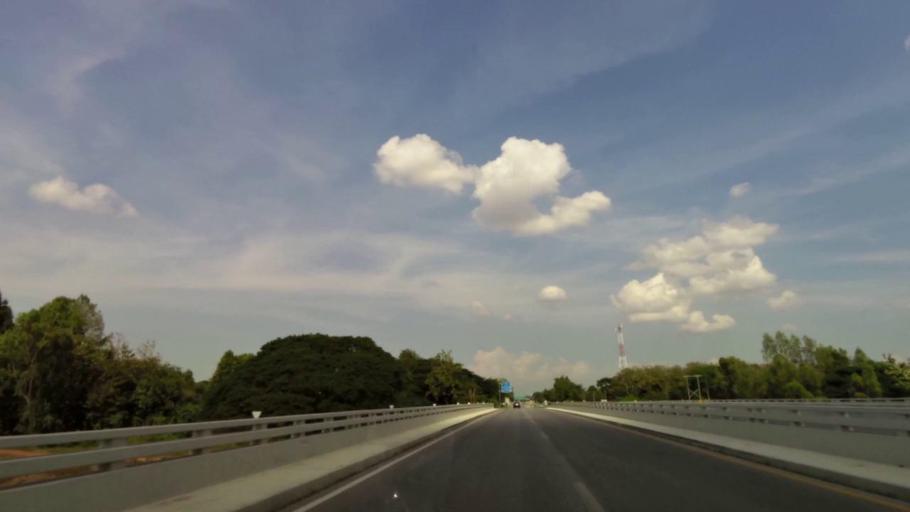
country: TH
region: Uttaradit
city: Thong Saen Khan
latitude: 17.4639
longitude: 100.2372
